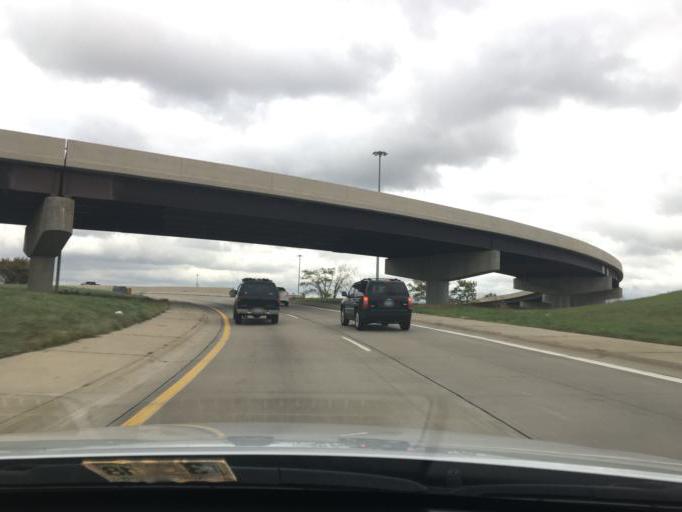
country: US
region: Michigan
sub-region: Macomb County
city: Center Line
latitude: 42.4868
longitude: -83.0481
